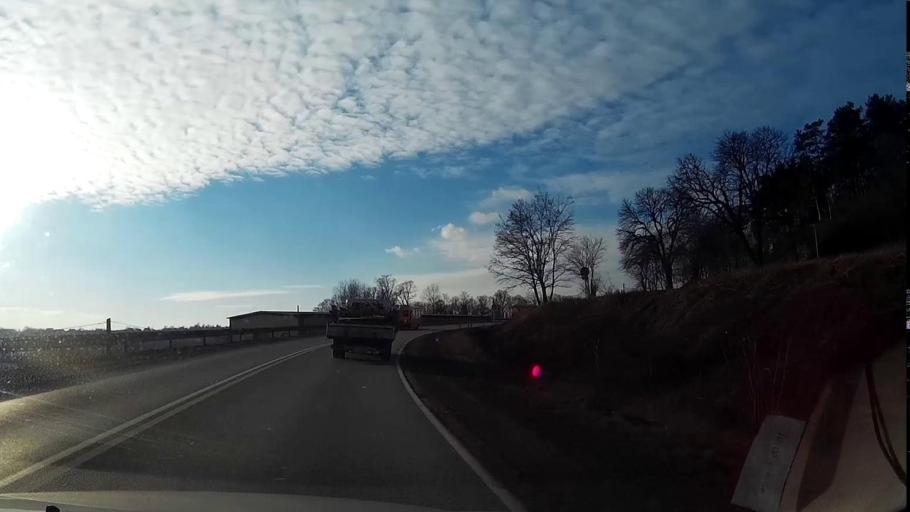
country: PL
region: Lesser Poland Voivodeship
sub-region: Powiat krakowski
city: Kryspinow
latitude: 50.0409
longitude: 19.8023
